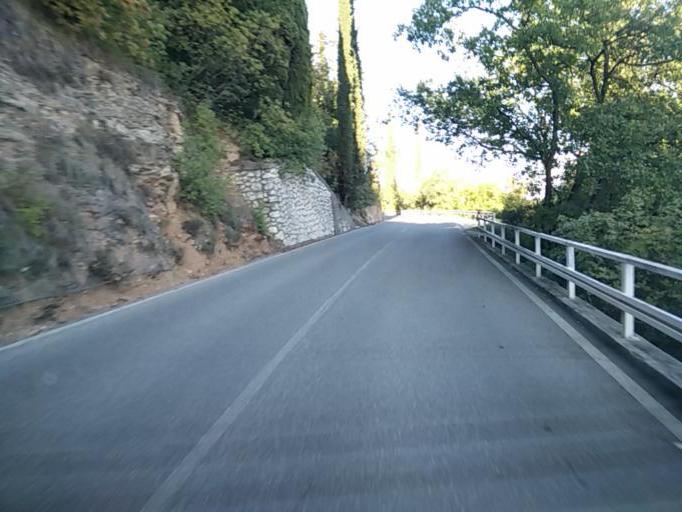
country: IT
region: Lombardy
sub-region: Provincia di Brescia
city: Gargnano
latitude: 45.6846
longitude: 10.6512
